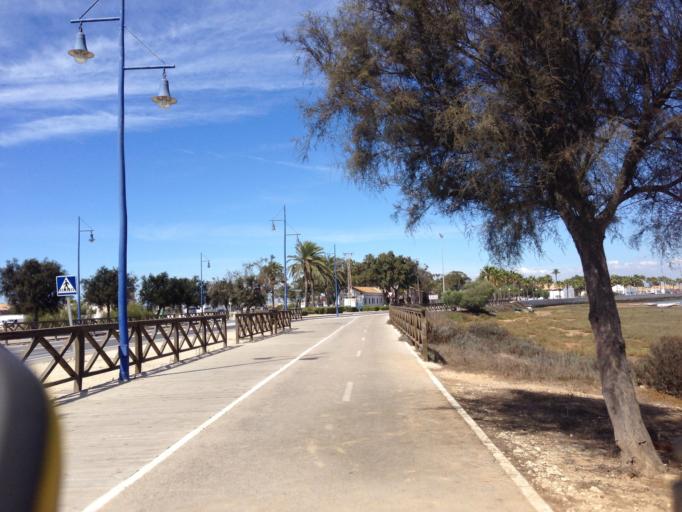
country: ES
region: Andalusia
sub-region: Provincia de Cadiz
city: Chiclana de la Frontera
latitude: 36.3918
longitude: -6.2073
